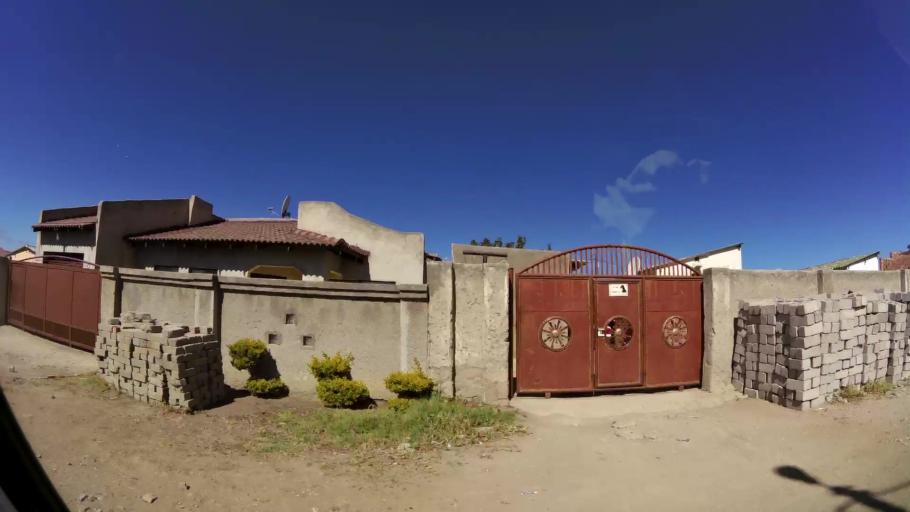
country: ZA
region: Limpopo
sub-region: Capricorn District Municipality
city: Polokwane
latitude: -23.8890
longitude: 29.4188
